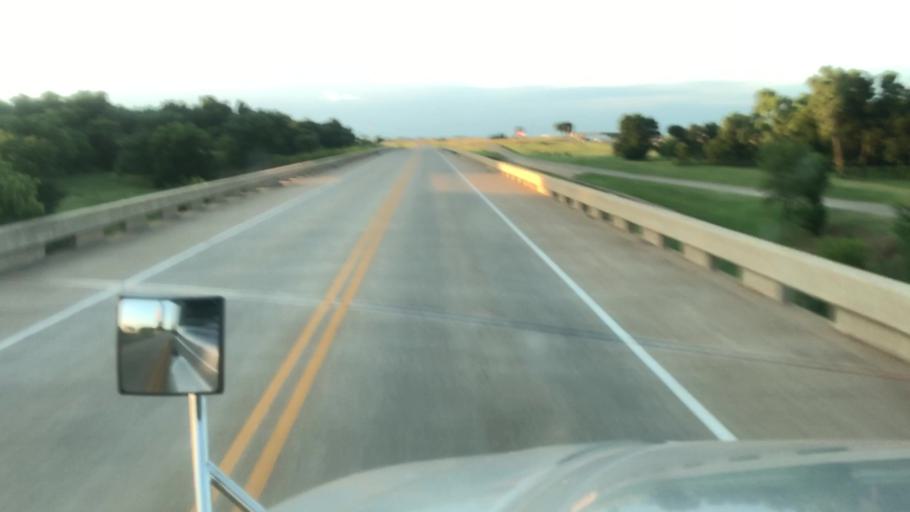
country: US
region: Oklahoma
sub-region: Osage County
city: McCord
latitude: 36.4943
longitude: -97.0736
